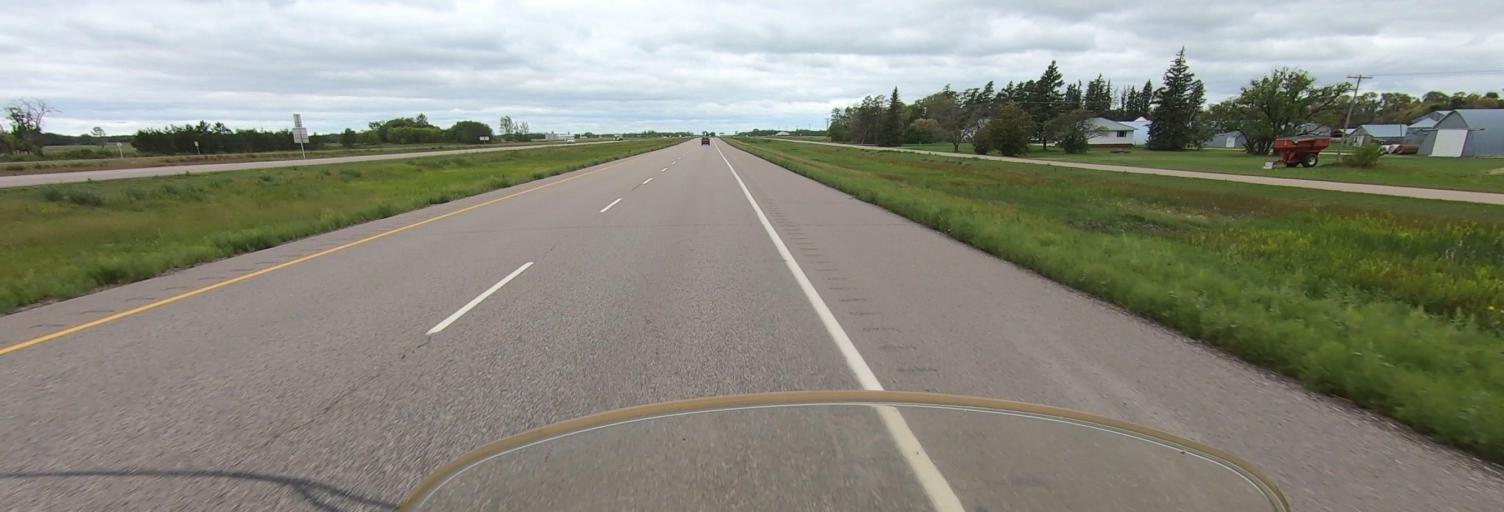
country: CA
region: Manitoba
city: Portage la Prairie
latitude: 49.9752
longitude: -98.6319
